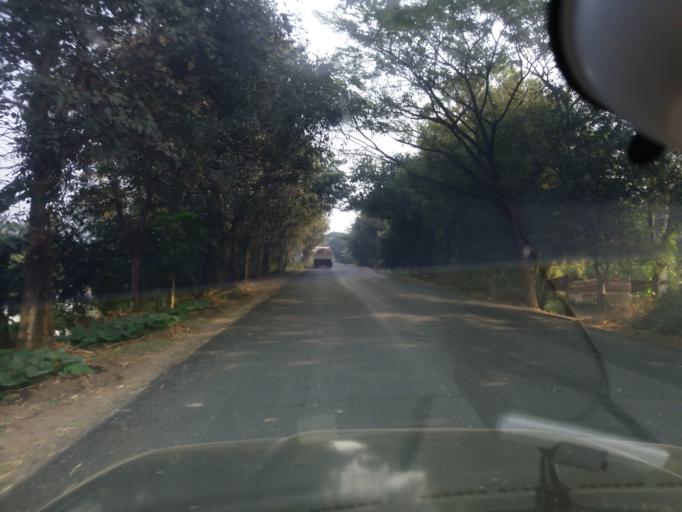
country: TH
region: Sing Buri
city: Bang Racham
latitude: 14.9048
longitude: 100.2276
